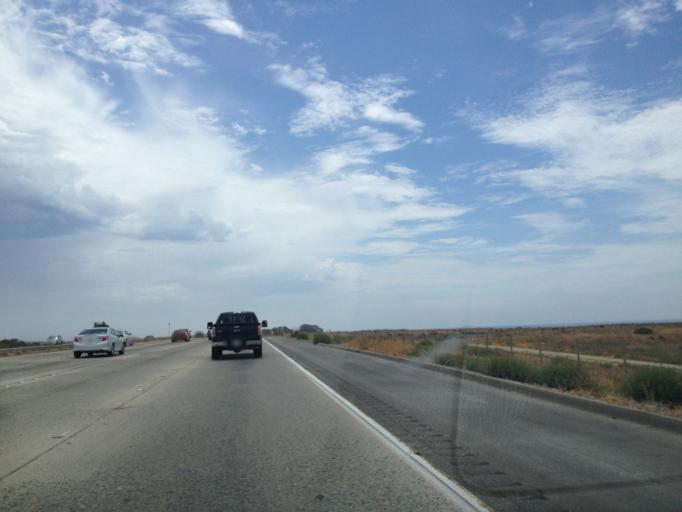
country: US
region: California
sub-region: San Diego County
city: Camp Pendleton South
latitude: 33.2852
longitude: -117.4524
